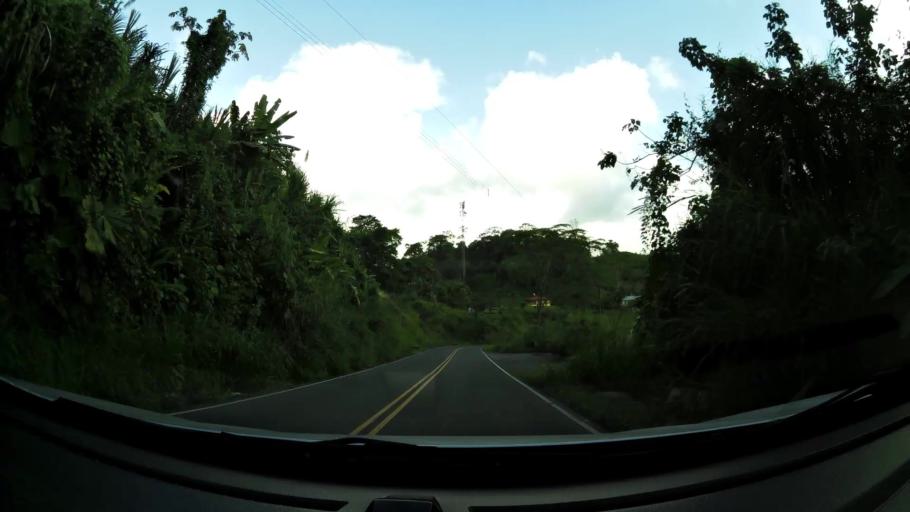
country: CR
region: Limon
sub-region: Canton de Siquirres
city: Siquirres
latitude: 10.0004
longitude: -83.5742
